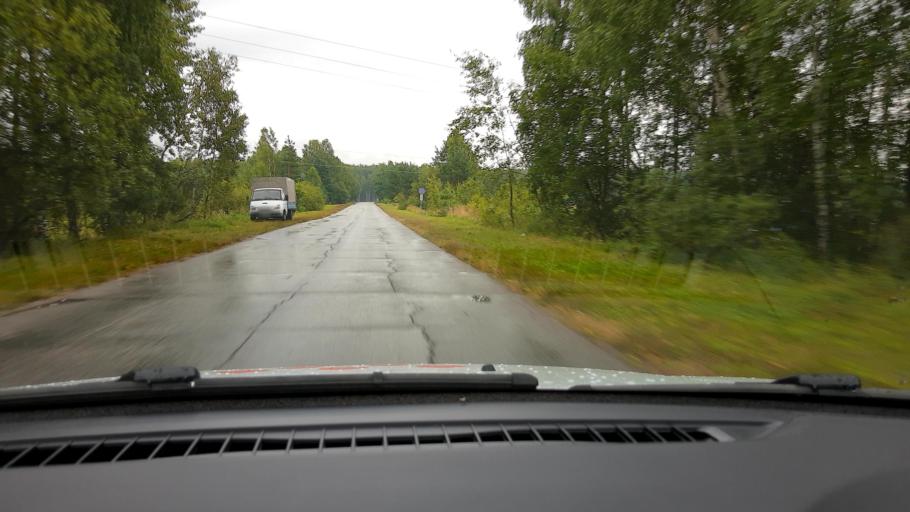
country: RU
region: Nizjnij Novgorod
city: Dal'neye Konstantinovo
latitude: 55.9495
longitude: 43.9707
